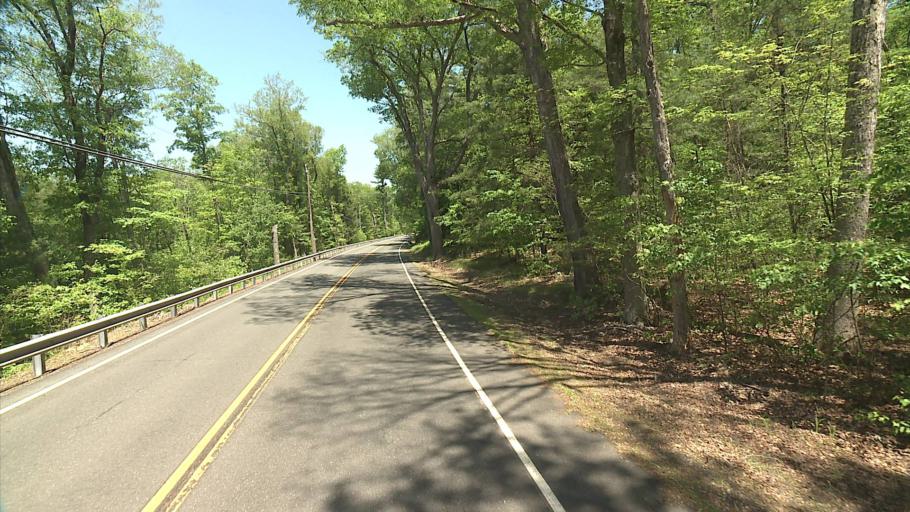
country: US
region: Connecticut
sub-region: Tolland County
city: Stafford
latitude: 42.0168
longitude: -72.2526
